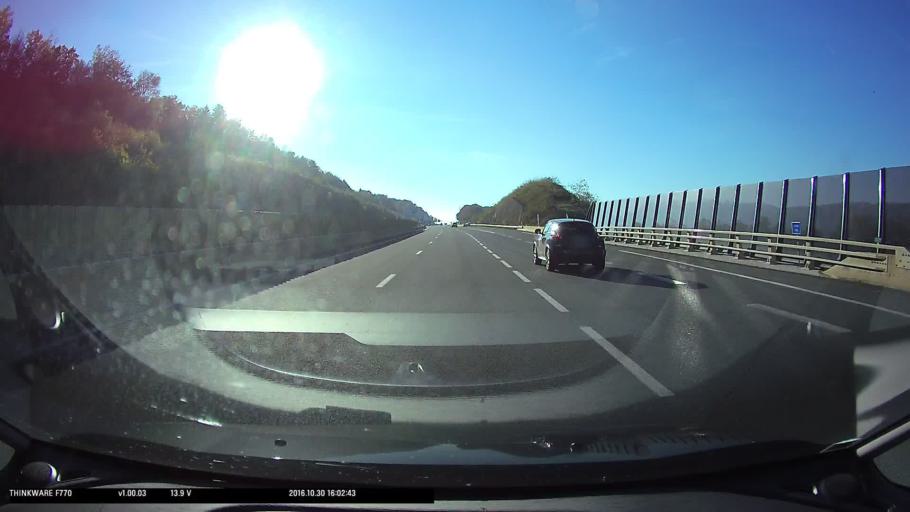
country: FR
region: Franche-Comte
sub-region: Departement du Doubs
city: Arbouans
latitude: 47.4842
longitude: 6.8046
